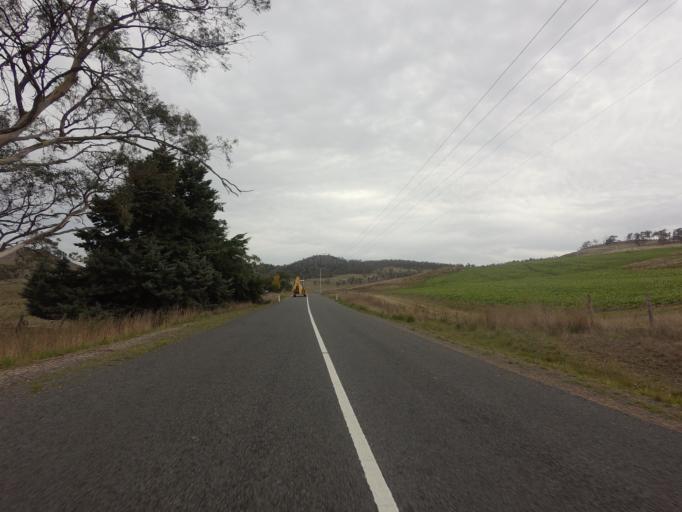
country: AU
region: Tasmania
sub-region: Derwent Valley
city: New Norfolk
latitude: -42.5137
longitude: 146.9544
